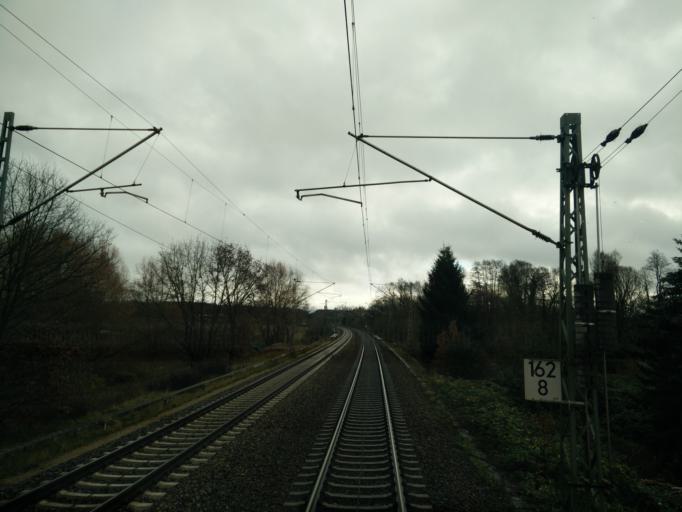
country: DE
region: Mecklenburg-Vorpommern
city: Grabow
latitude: 53.2824
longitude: 11.5649
